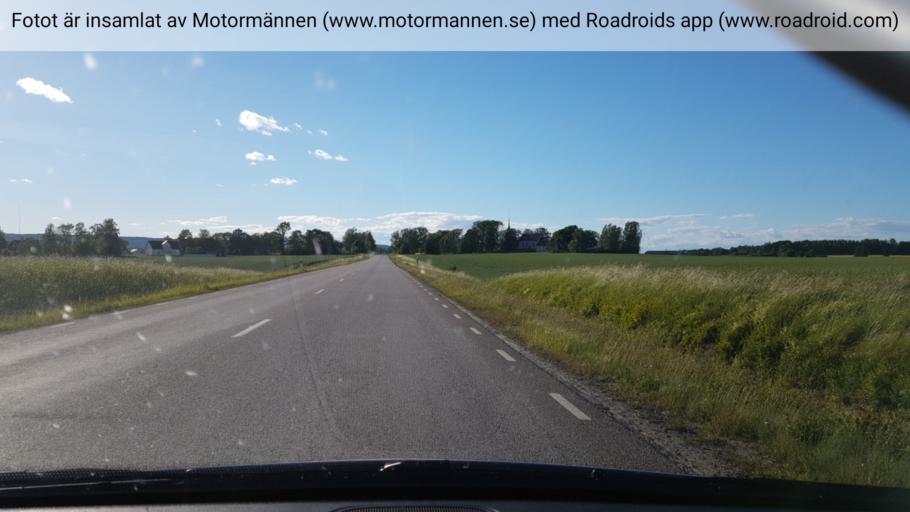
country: SE
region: Vaestra Goetaland
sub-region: Skovde Kommun
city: Skoevde
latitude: 58.3858
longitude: 13.9423
